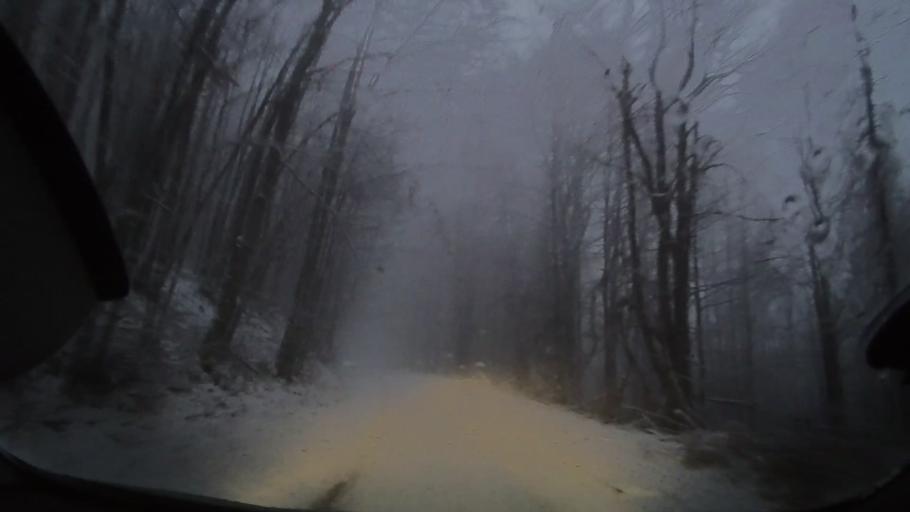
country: RO
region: Alba
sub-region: Comuna Avram Iancu
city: Avram Iancu
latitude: 46.3131
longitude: 22.8048
